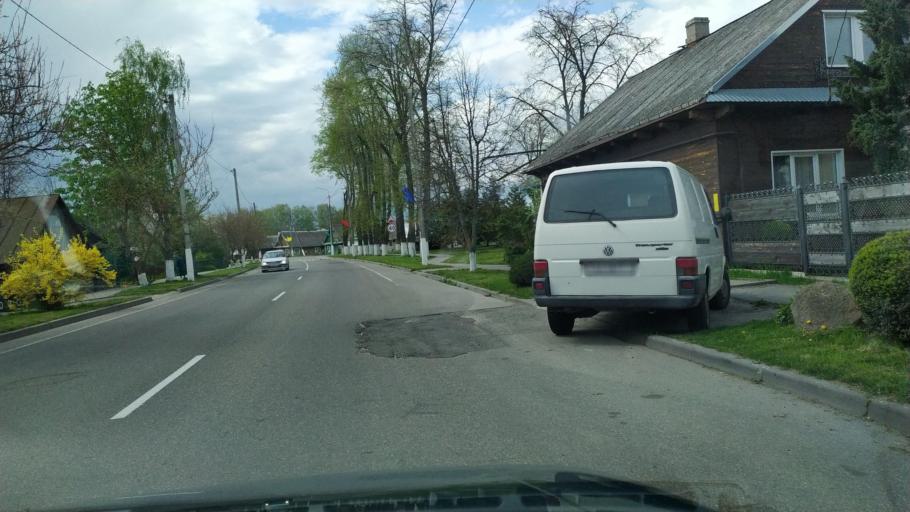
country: BY
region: Brest
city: Pruzhany
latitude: 52.5562
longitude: 24.4522
